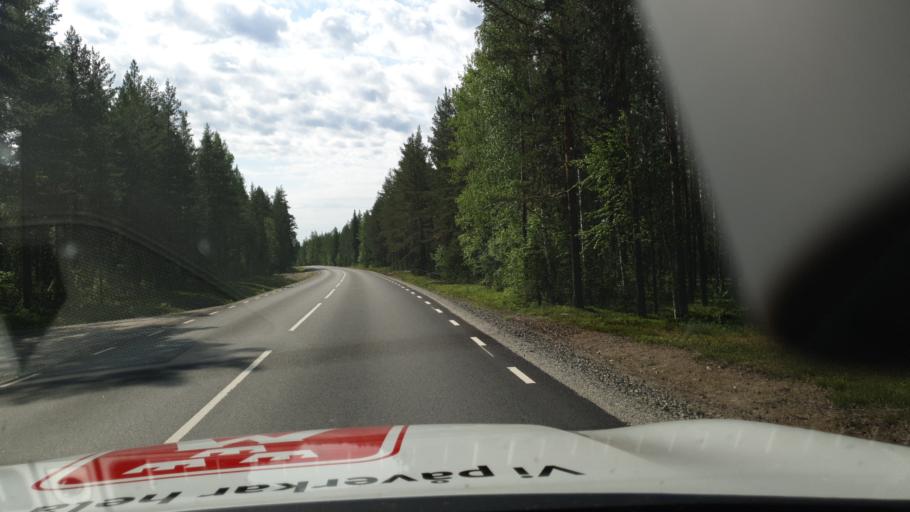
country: SE
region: Vaesterbotten
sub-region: Norsjo Kommun
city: Norsjoe
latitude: 64.6169
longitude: 19.2893
